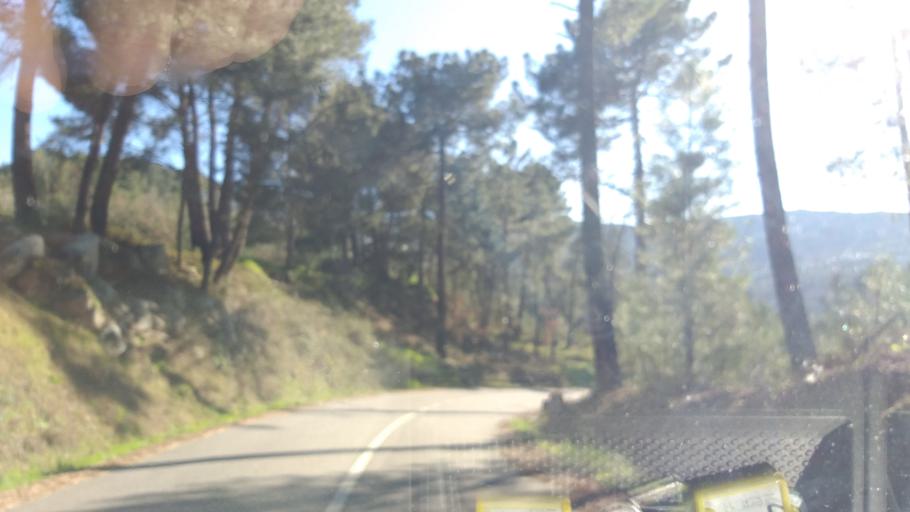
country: PT
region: Guarda
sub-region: Celorico da Beira
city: Celorico da Beira
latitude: 40.5903
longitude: -7.3605
